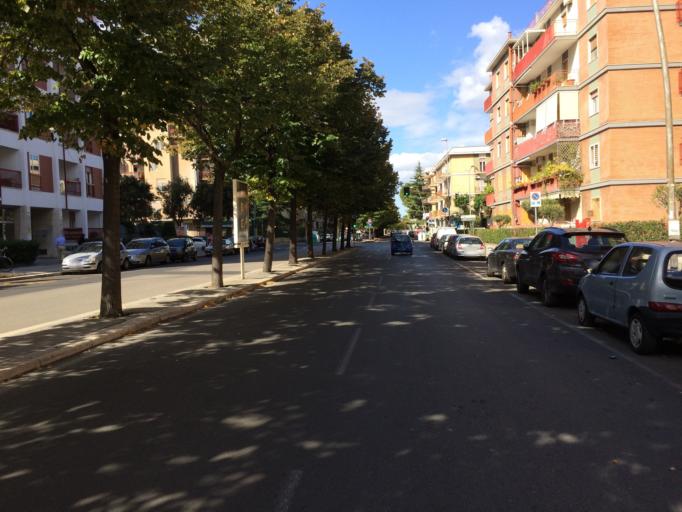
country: IT
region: Apulia
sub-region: Provincia di Bari
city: Bari
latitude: 41.1011
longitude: 16.8658
